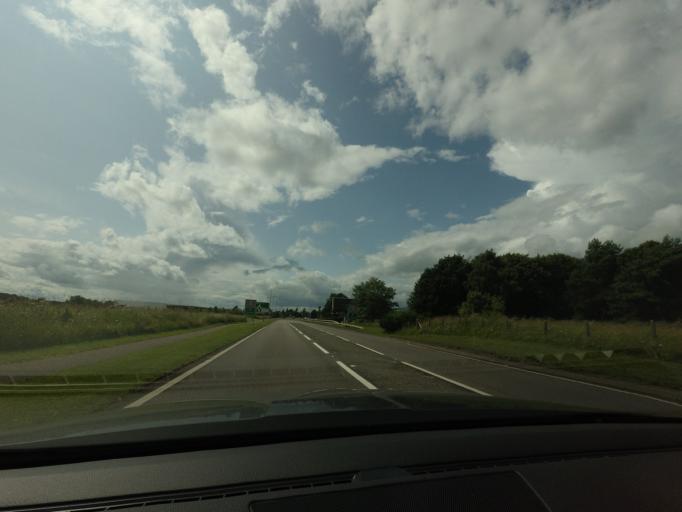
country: GB
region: Scotland
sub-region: Highland
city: Nairn
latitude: 57.5827
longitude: -3.8469
